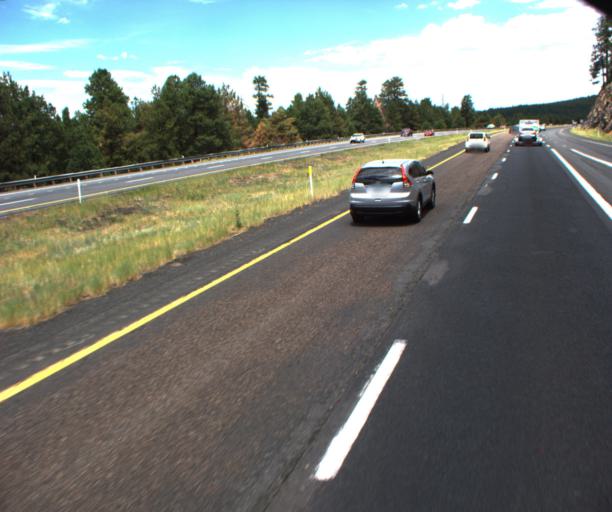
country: US
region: Arizona
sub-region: Coconino County
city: Mountainaire
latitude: 35.0560
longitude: -111.6835
